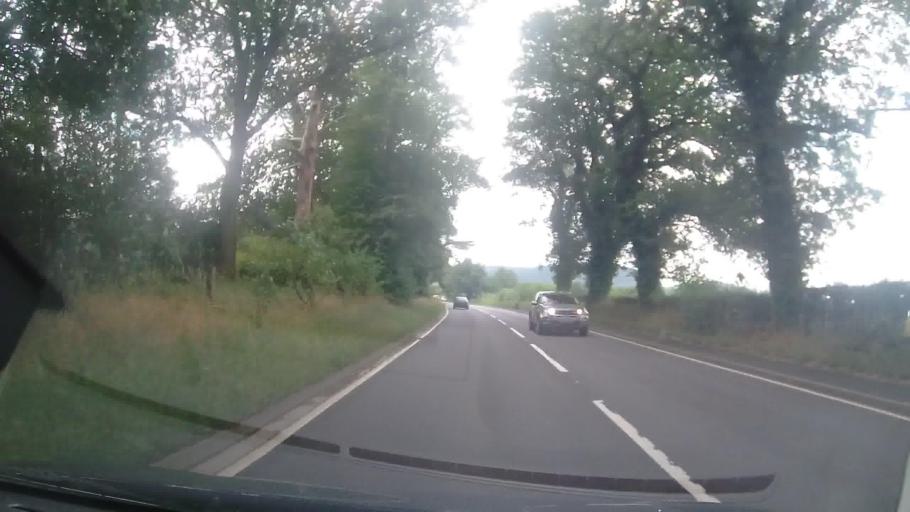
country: GB
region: England
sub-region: Shropshire
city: Craven Arms
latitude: 52.4501
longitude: -2.8379
